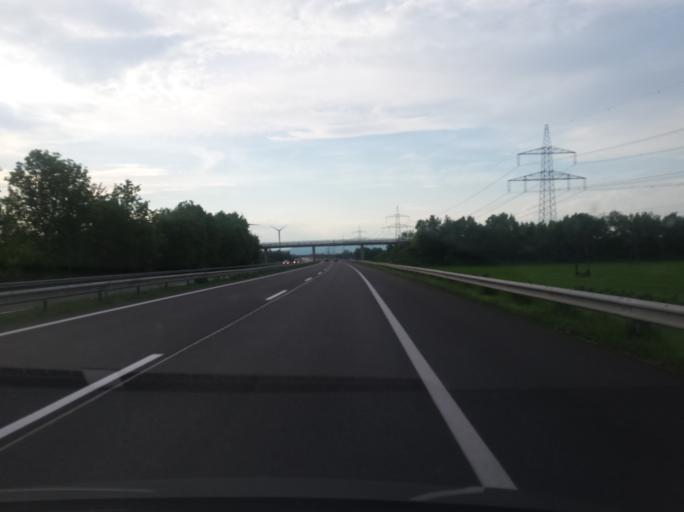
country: AT
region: Lower Austria
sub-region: Politischer Bezirk Baden
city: Ebreichsdorf
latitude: 47.9234
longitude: 16.3985
